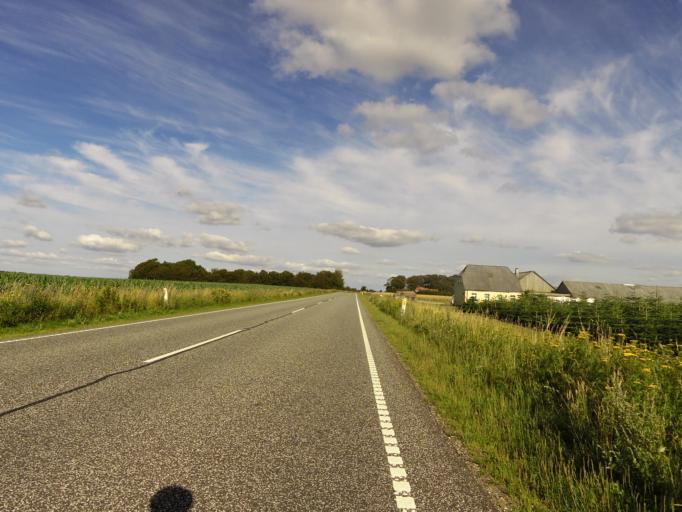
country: DK
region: South Denmark
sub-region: Haderslev Kommune
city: Gram
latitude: 55.2302
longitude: 8.9780
